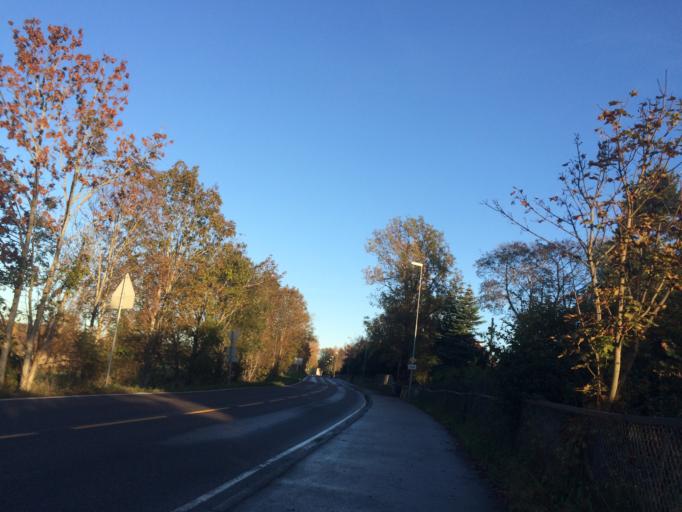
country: NO
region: Akershus
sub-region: Ski
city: Ski
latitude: 59.7215
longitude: 10.8475
